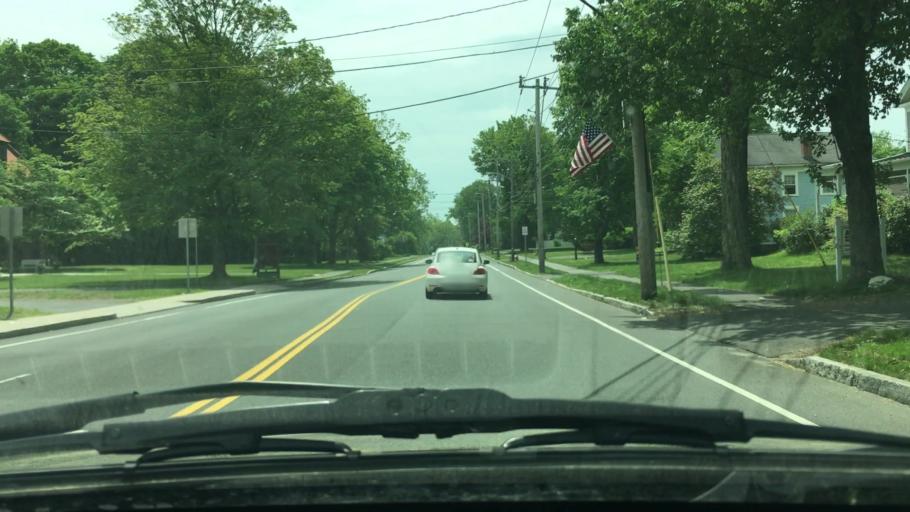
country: US
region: Massachusetts
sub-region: Hampshire County
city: Belchertown
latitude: 42.2764
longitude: -72.4006
